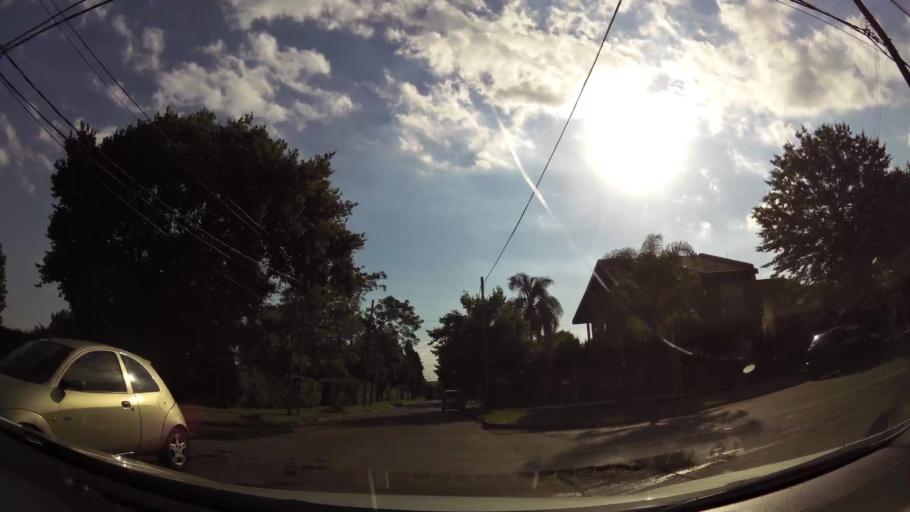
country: AR
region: Buenos Aires
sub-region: Partido de Tigre
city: Tigre
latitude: -34.4721
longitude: -58.6534
